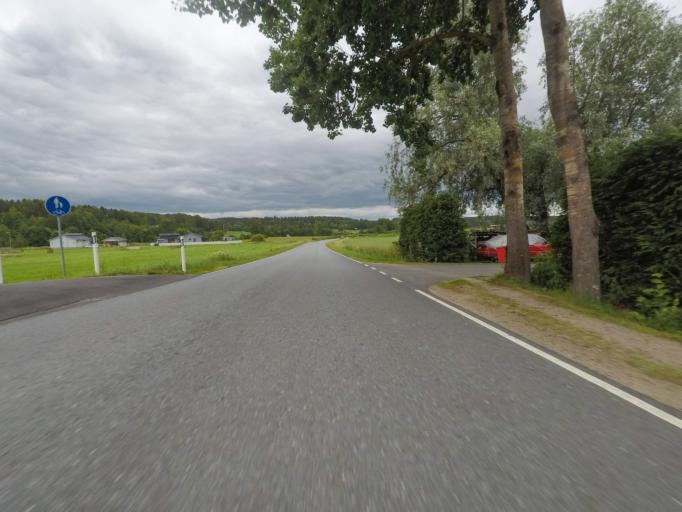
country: FI
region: Varsinais-Suomi
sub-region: Salo
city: Muurla
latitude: 60.3489
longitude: 23.2826
